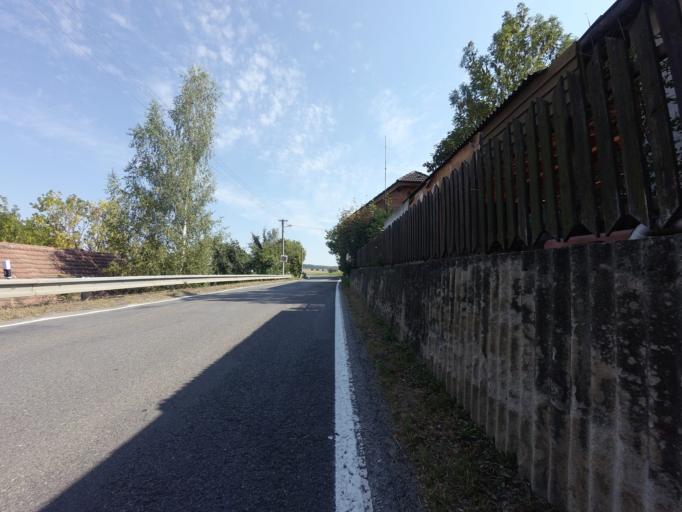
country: CZ
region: Jihocesky
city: Bernartice
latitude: 49.3916
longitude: 14.3593
